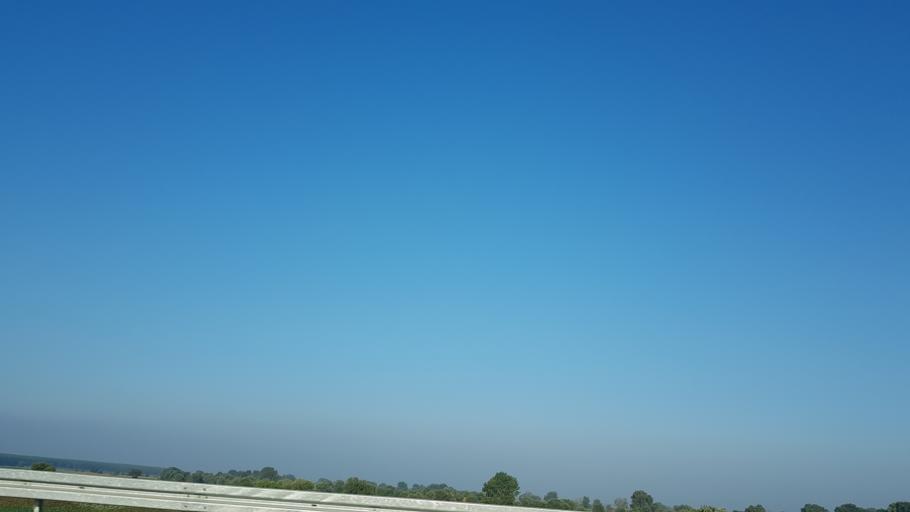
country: TR
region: Bursa
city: Tatkavakli
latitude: 40.1086
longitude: 28.2772
